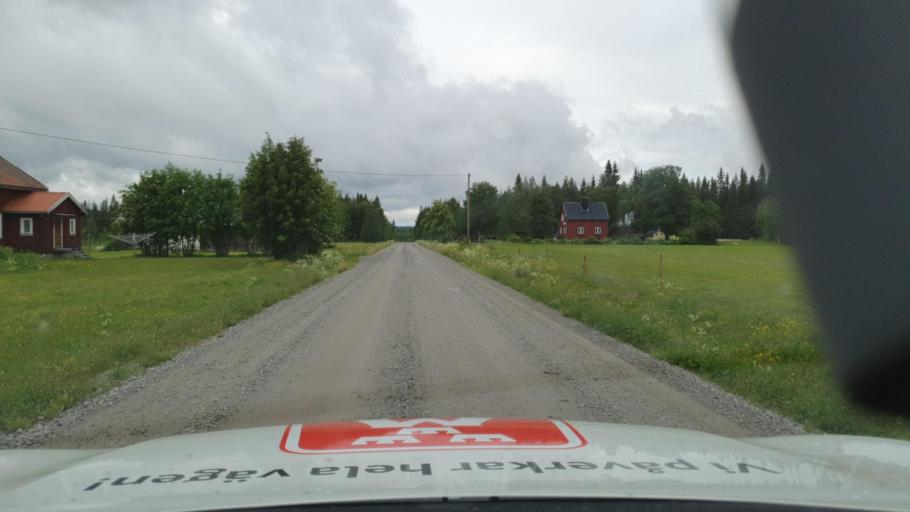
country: SE
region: Vaesterbotten
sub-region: Dorotea Kommun
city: Dorotea
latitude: 64.0827
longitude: 16.6837
